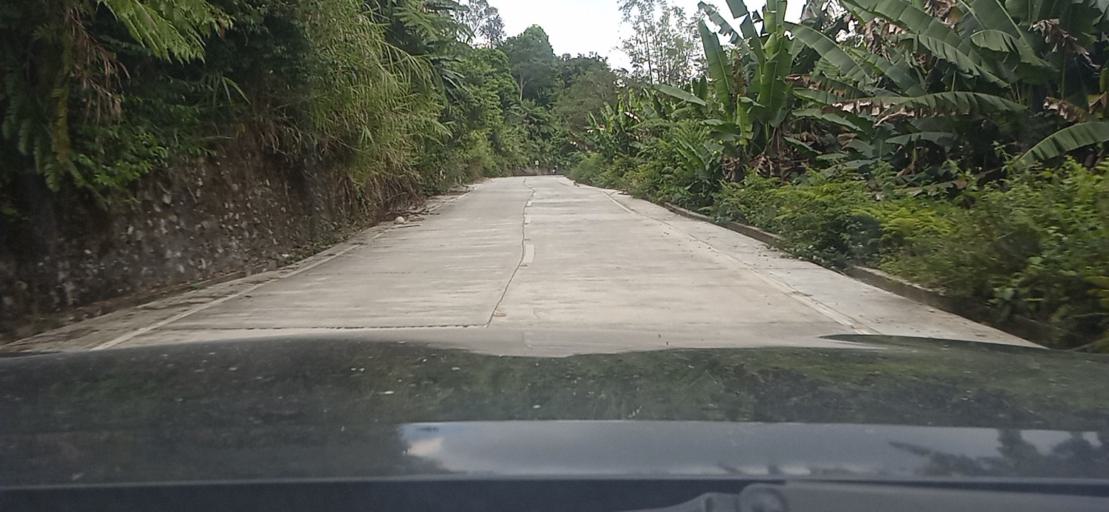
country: PH
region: Cordillera
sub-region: Kalinga
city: Lubuagan
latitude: 17.3746
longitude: 121.1812
